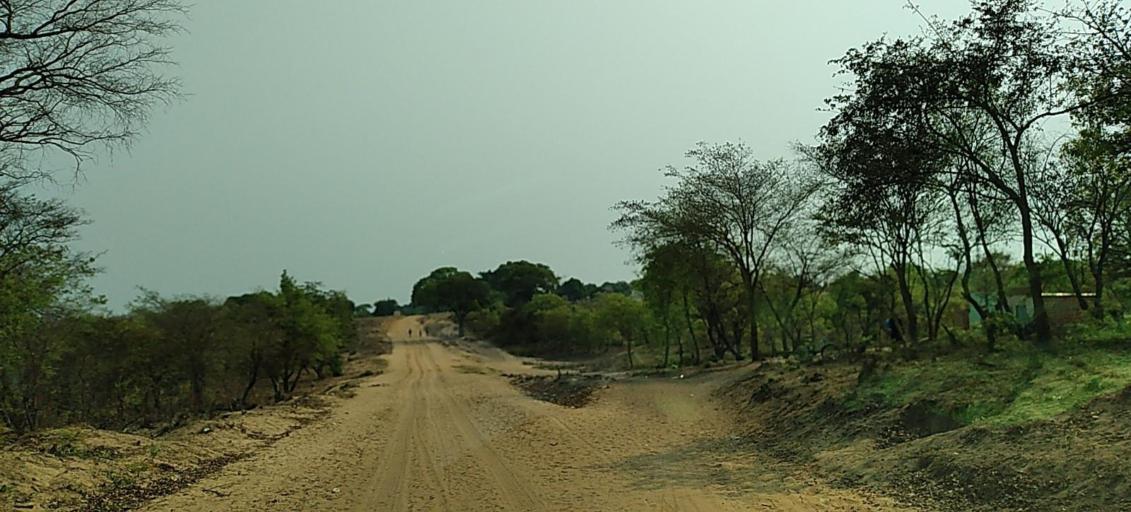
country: ZM
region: North-Western
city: Zambezi
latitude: -13.1783
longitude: 23.4014
